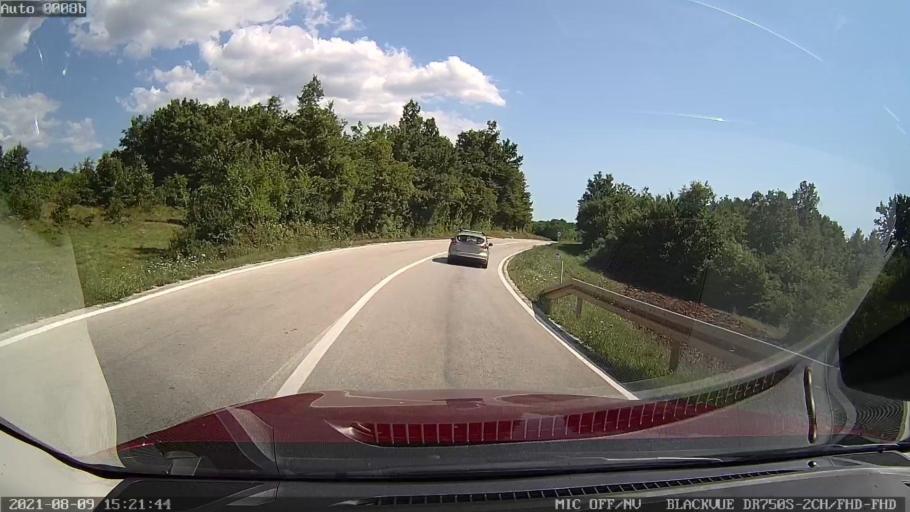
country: HR
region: Istarska
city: Pazin
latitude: 45.1968
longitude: 13.8985
